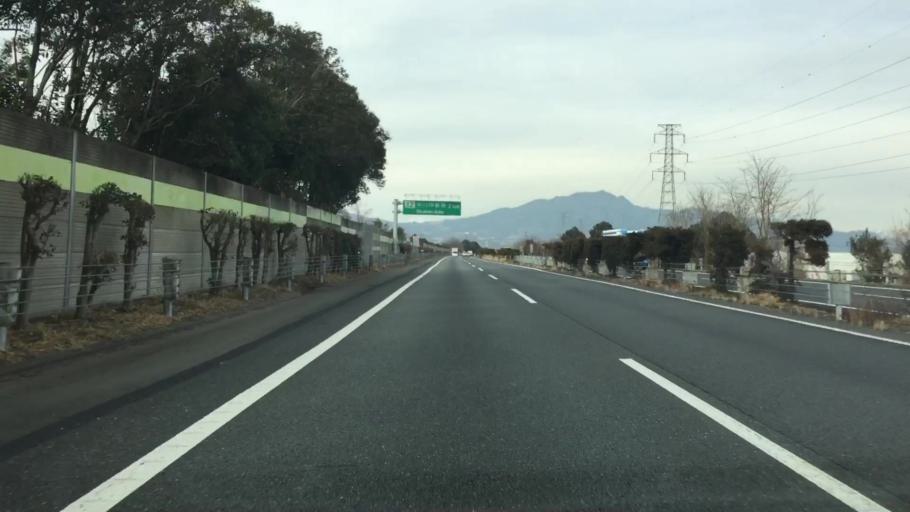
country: JP
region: Gunma
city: Shibukawa
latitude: 36.4561
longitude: 139.0133
